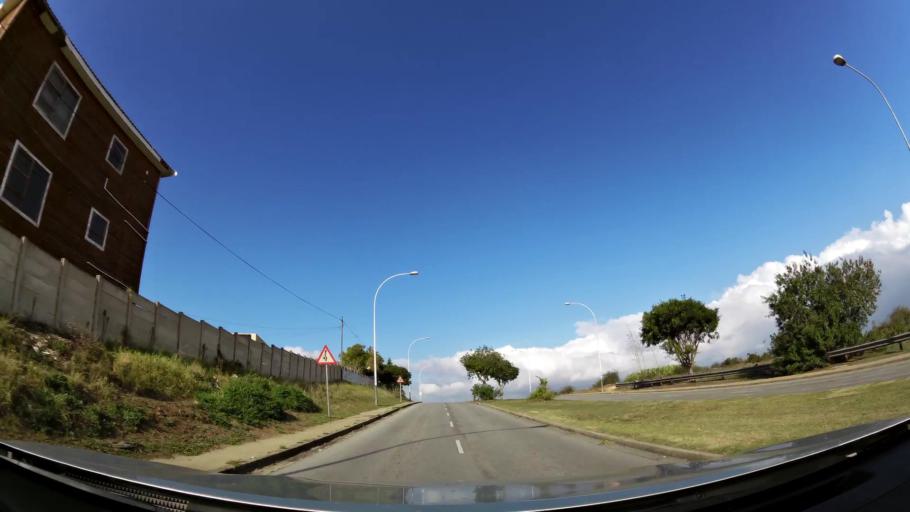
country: ZA
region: Eastern Cape
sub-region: Nelson Mandela Bay Metropolitan Municipality
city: Uitenhage
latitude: -33.7709
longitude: 25.4267
